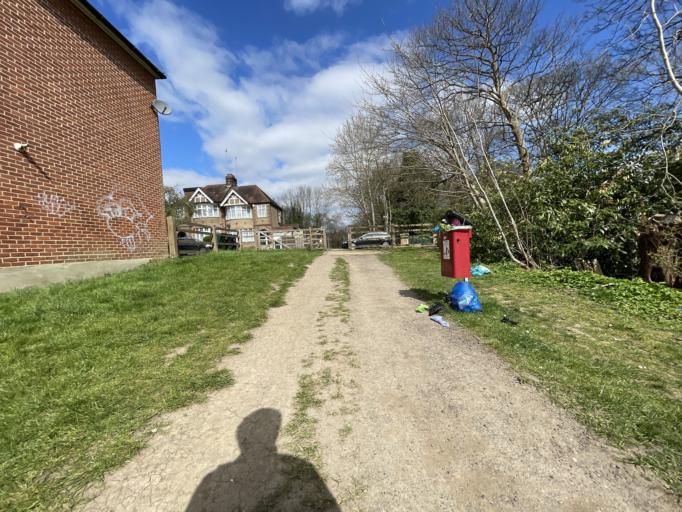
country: GB
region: England
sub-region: Greater London
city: Barnet
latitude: 51.6232
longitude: -0.1860
